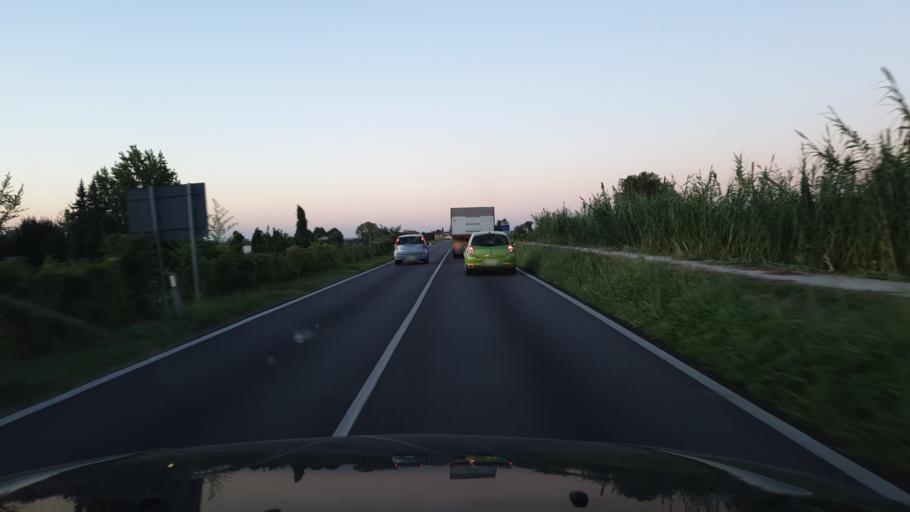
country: IT
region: Emilia-Romagna
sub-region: Provincia di Bologna
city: Ca De Fabbri
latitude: 44.6217
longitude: 11.4557
